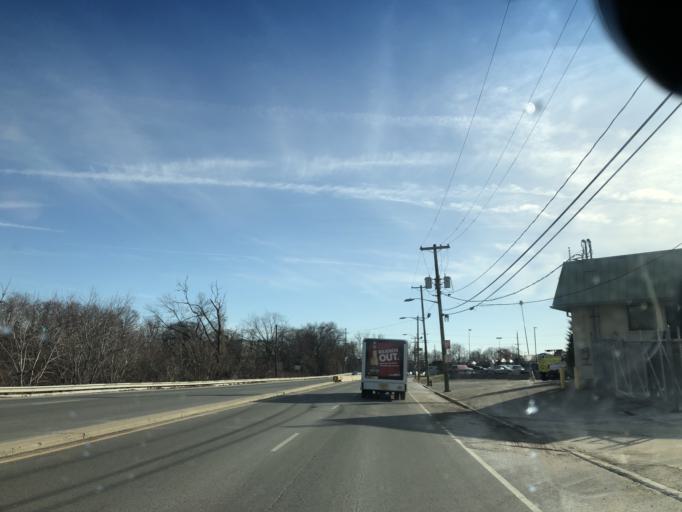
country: US
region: New Jersey
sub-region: Bergen County
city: Fair Lawn
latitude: 40.9360
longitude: -74.1414
